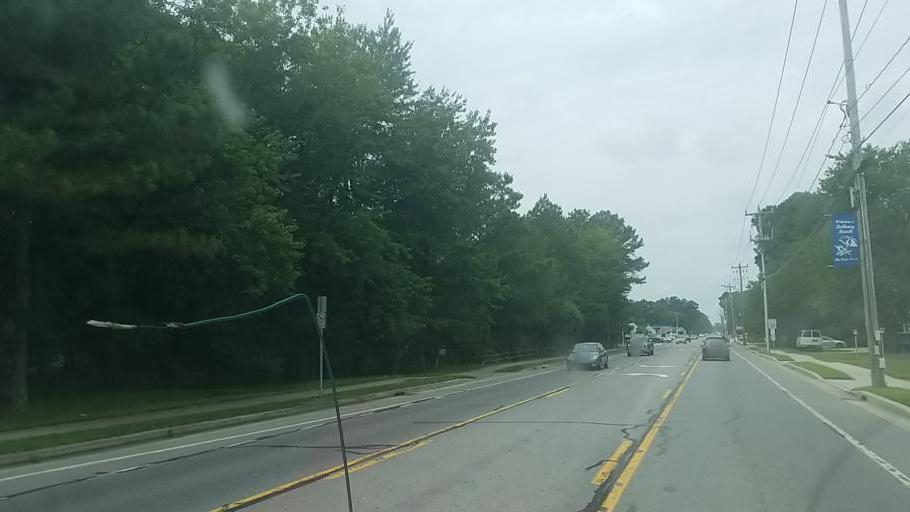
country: US
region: Delaware
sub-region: Sussex County
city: Bethany Beach
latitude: 38.5398
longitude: -75.0686
